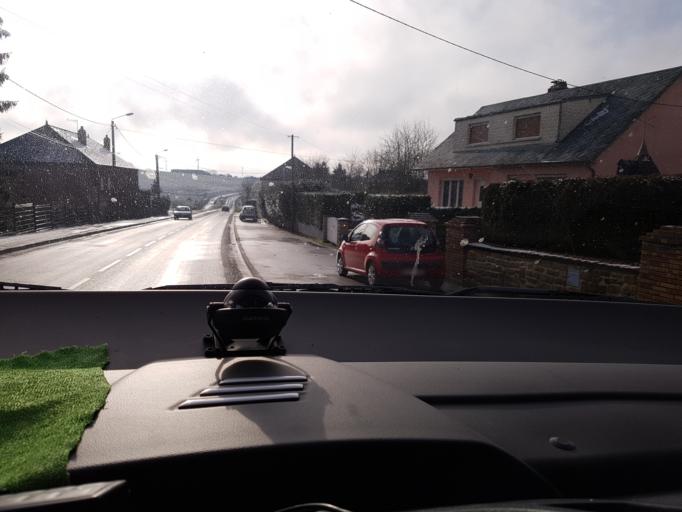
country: FR
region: Champagne-Ardenne
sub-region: Departement des Ardennes
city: Signy-le-Petit
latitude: 49.8691
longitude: 4.3731
